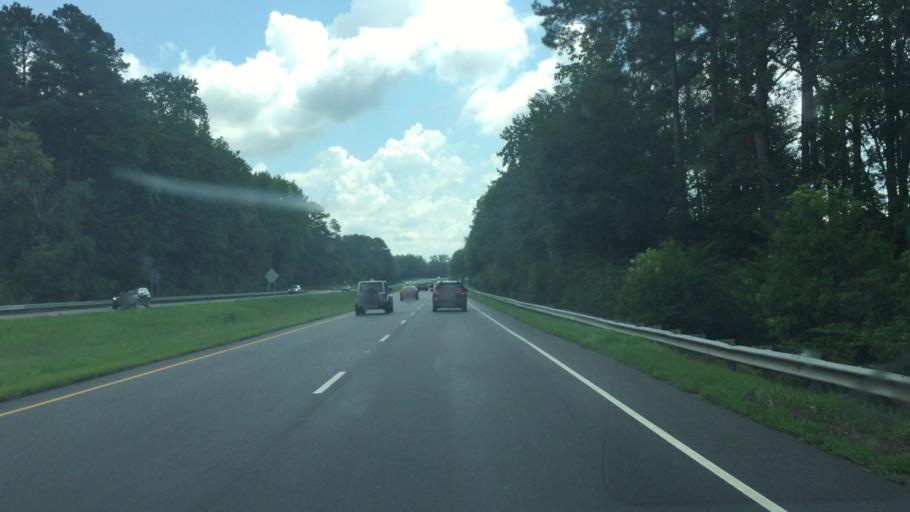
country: US
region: North Carolina
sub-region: Scotland County
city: Laurel Hill
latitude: 34.7994
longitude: -79.5307
